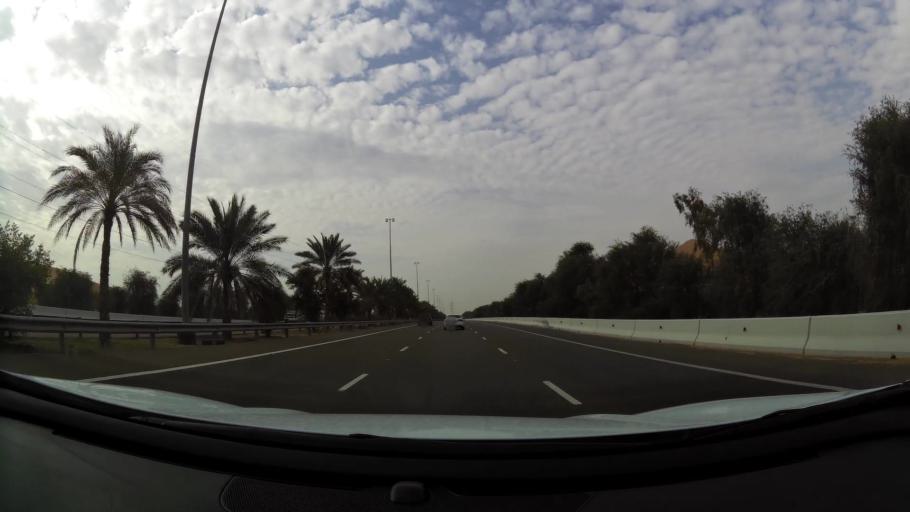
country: AE
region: Abu Dhabi
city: Al Ain
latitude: 24.2161
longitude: 55.5670
